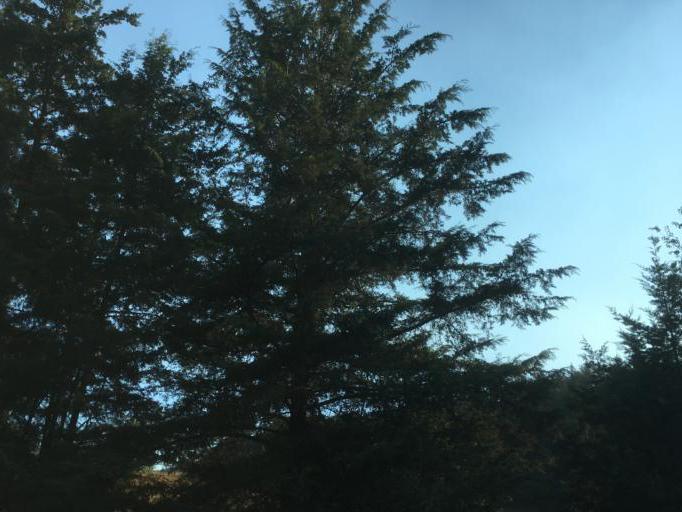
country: MX
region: Michoacan
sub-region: Morelia
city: Iratzio
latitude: 19.6216
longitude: -101.4621
